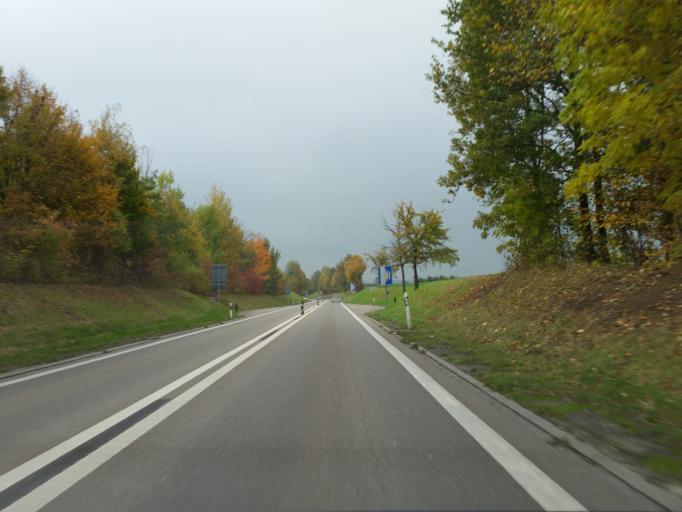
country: CH
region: Thurgau
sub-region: Arbon District
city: Egnach
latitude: 47.5276
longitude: 9.3988
